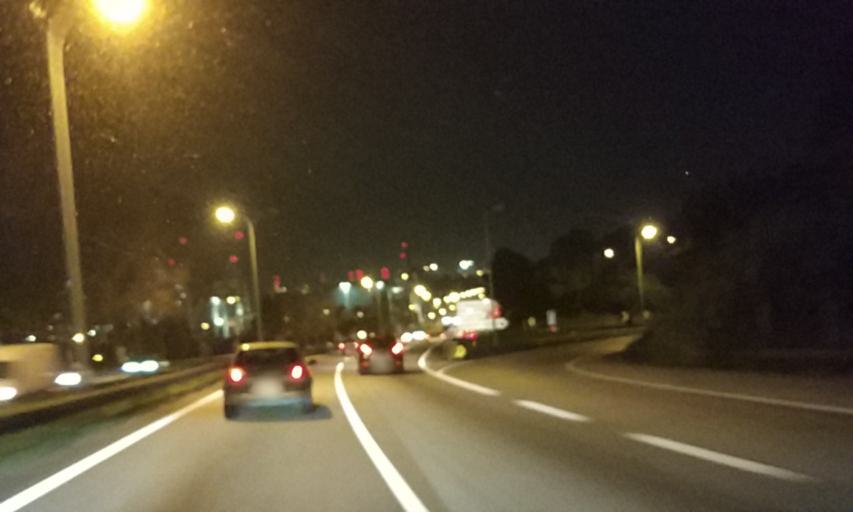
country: PT
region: Porto
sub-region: Matosinhos
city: Guifoes
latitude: 41.1917
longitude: -8.6767
